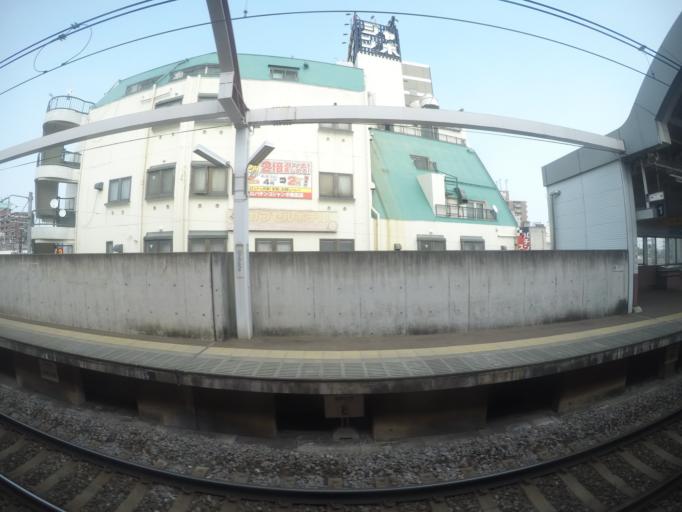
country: JP
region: Aichi
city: Obu
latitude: 35.0724
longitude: 136.9093
